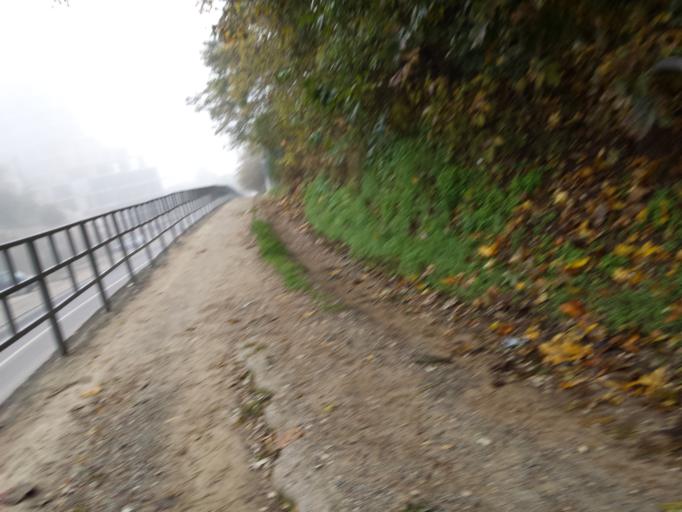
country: RO
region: Cluj
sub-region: Municipiul Cluj-Napoca
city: Cluj-Napoca
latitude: 46.7767
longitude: 23.5612
